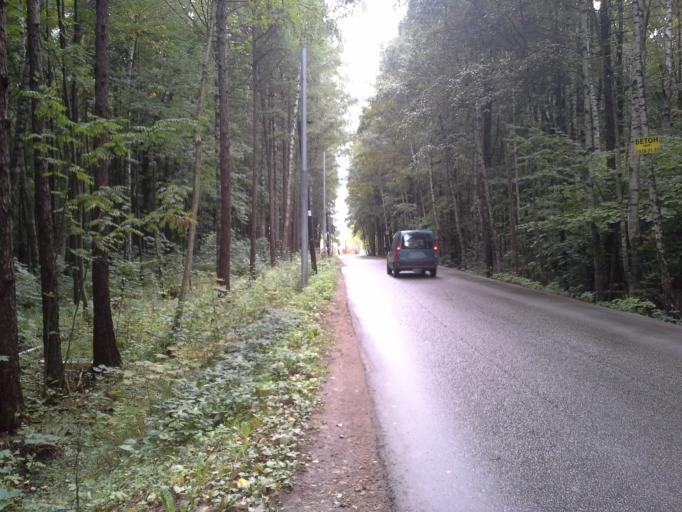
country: RU
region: Moskovskaya
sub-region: Leninskiy Rayon
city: Vnukovo
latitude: 55.6410
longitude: 37.2744
